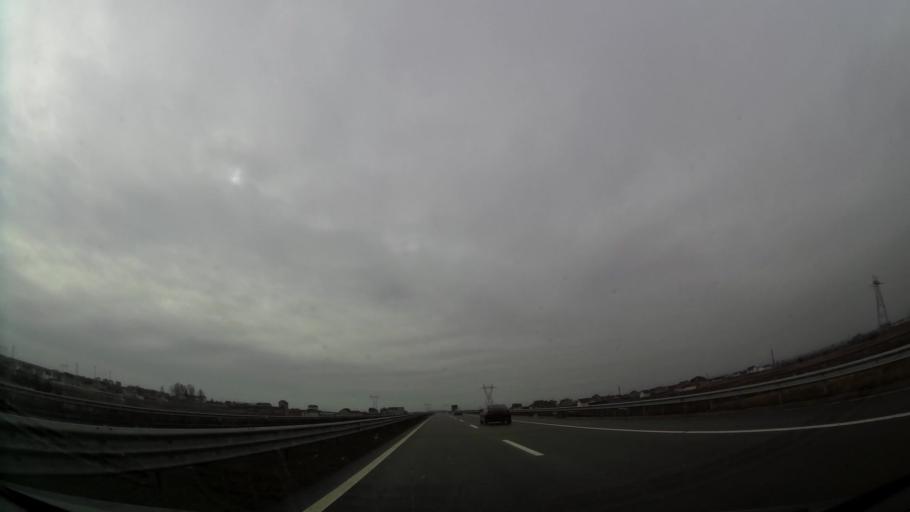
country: XK
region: Pristina
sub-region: Lipjan
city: Lipljan
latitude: 42.4762
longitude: 21.1833
